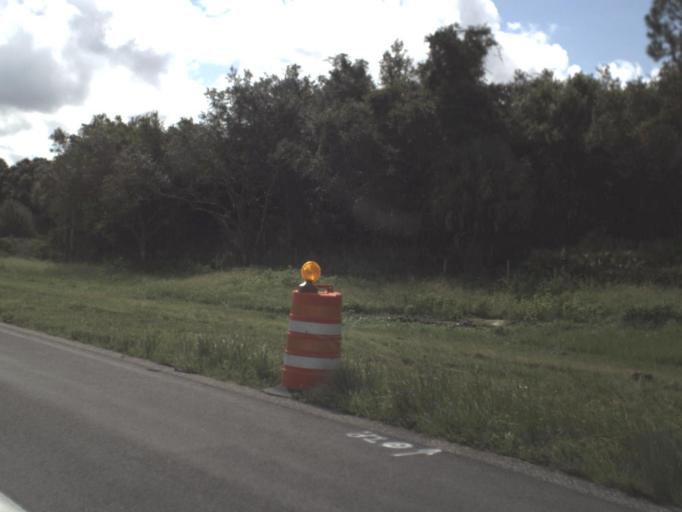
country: US
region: Florida
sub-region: Sarasota County
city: North Port
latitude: 27.0992
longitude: -82.2147
